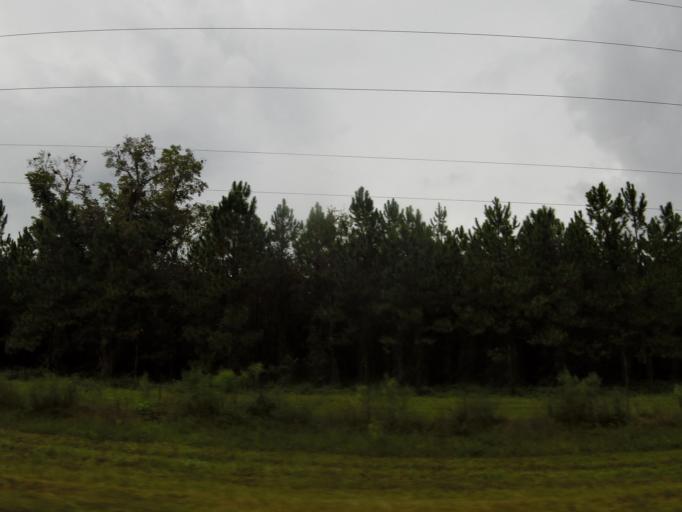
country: US
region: Florida
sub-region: Duval County
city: Baldwin
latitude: 30.4974
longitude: -82.0381
